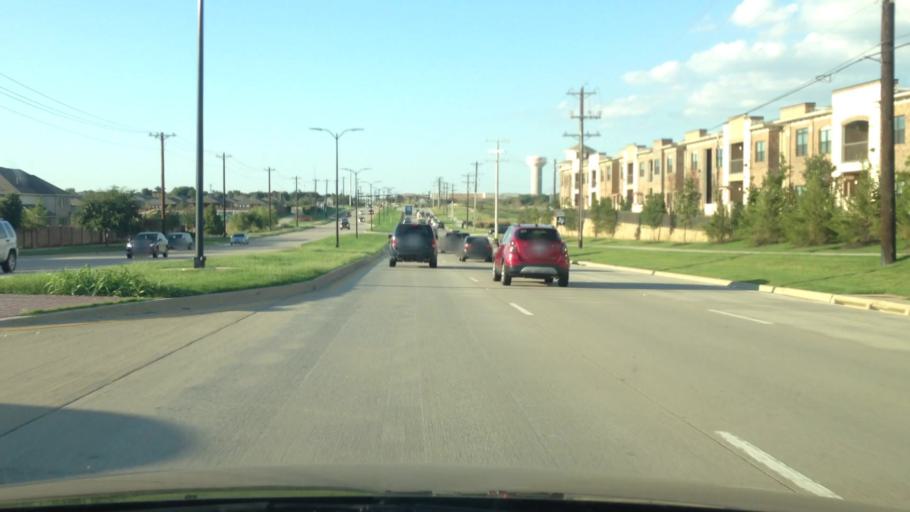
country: US
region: Texas
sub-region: Denton County
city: The Colony
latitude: 33.1315
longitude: -96.8908
